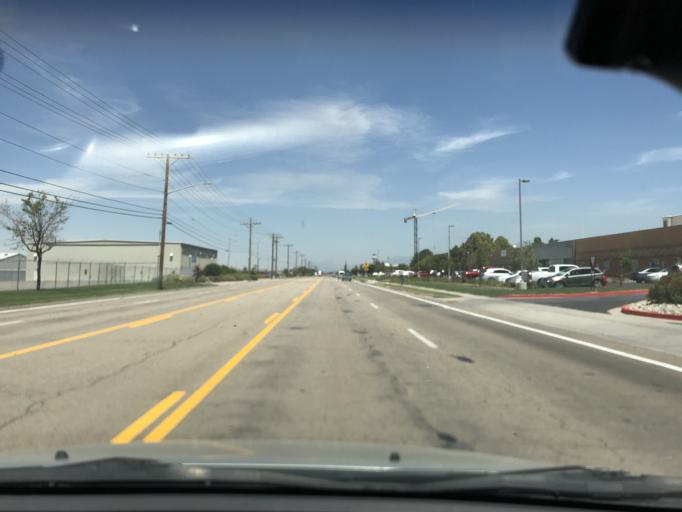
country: US
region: Utah
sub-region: Salt Lake County
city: Salt Lake City
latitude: 40.7776
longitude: -111.9535
